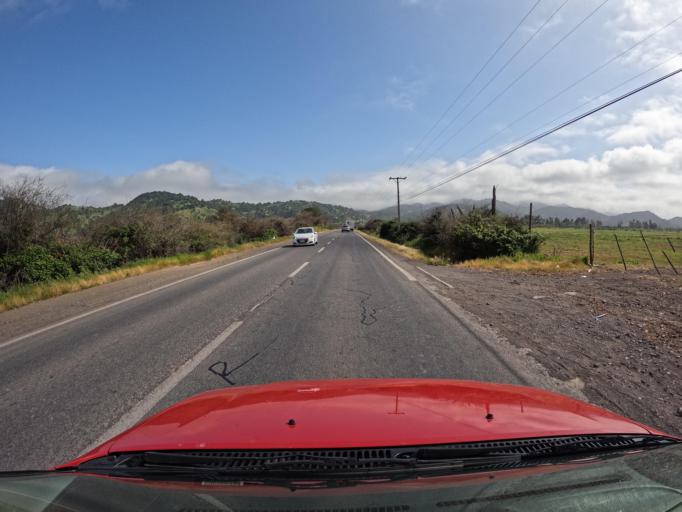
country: CL
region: Maule
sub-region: Provincia de Curico
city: Teno
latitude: -34.8355
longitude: -71.1886
